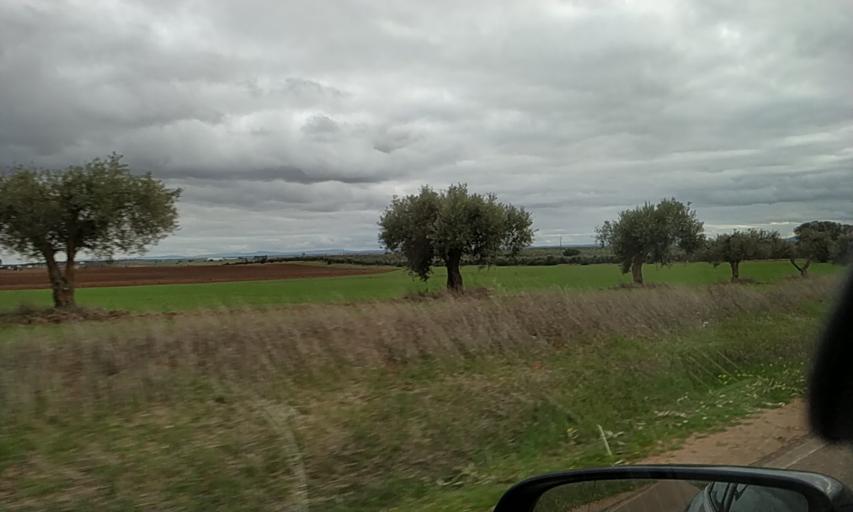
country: PT
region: Portalegre
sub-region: Campo Maior
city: Campo Maior
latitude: 38.9548
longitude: -7.0359
